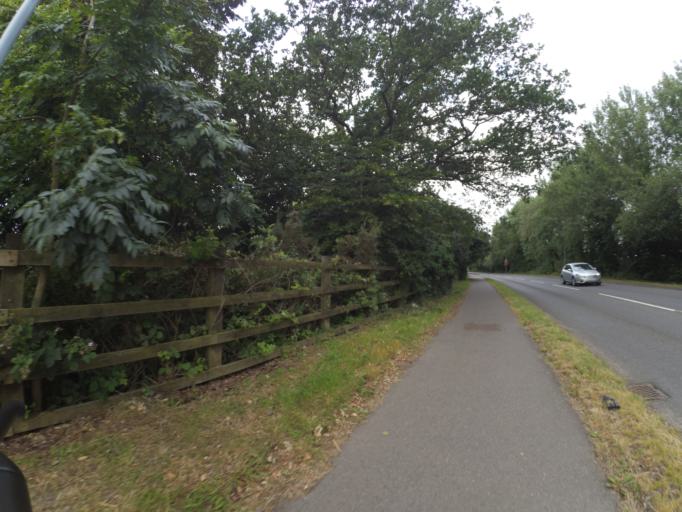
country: GB
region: England
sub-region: Warwickshire
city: Dunchurch
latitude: 52.3476
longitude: -1.2707
